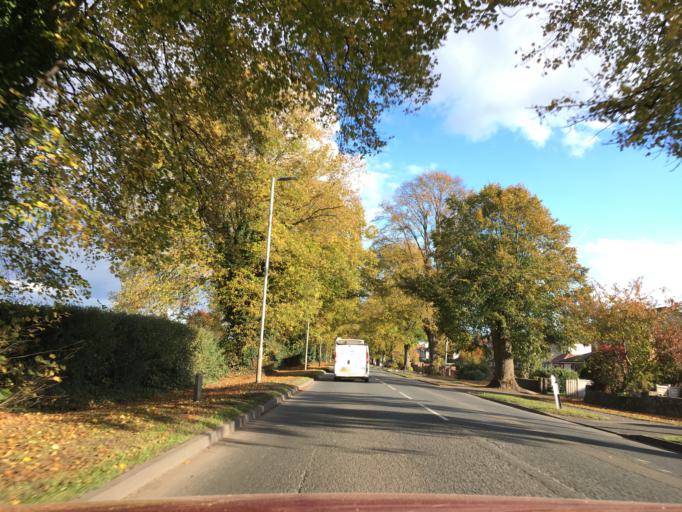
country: GB
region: England
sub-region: Herefordshire
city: Belmont
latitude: 52.0668
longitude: -2.7602
